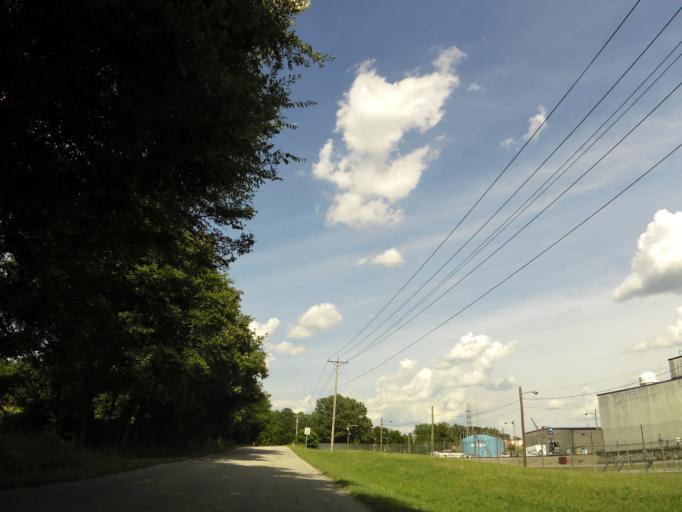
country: US
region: Tennessee
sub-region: Carroll County
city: Huntingdon
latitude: 36.0200
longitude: -88.3835
